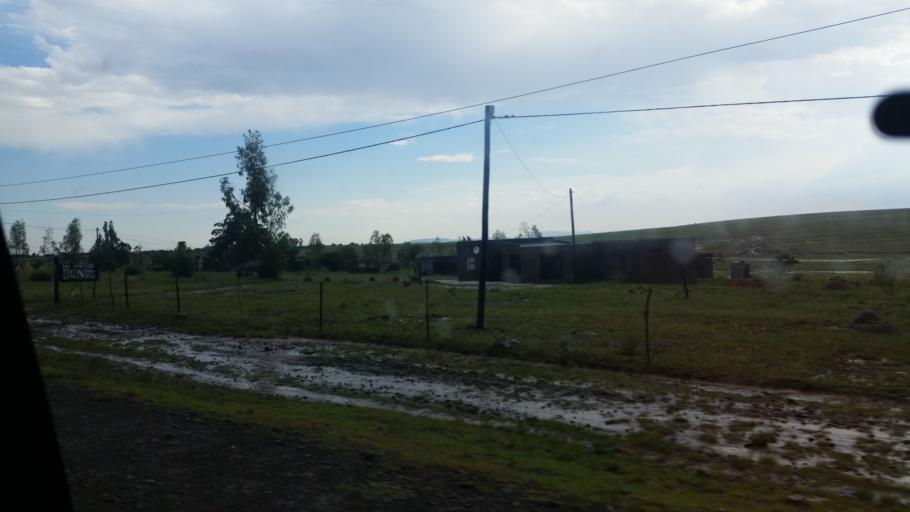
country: LS
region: Mafeteng
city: Mafeteng
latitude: -29.7630
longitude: 27.1752
